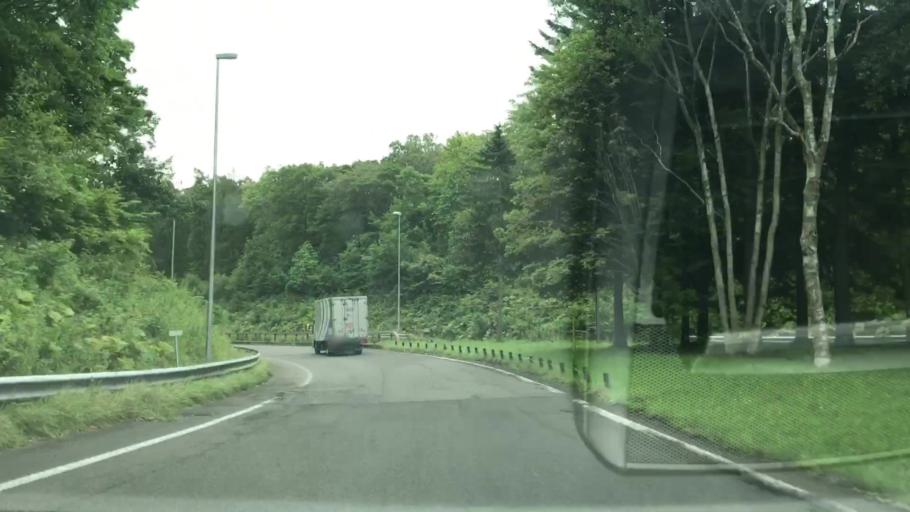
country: JP
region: Hokkaido
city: Chitose
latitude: 42.8114
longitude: 141.6264
